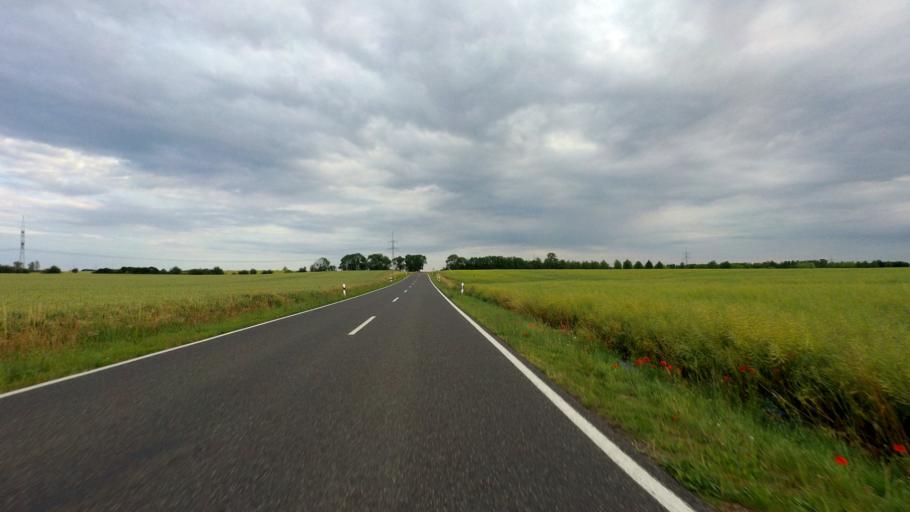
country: DE
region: Brandenburg
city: Pawesin
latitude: 52.5675
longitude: 12.7677
